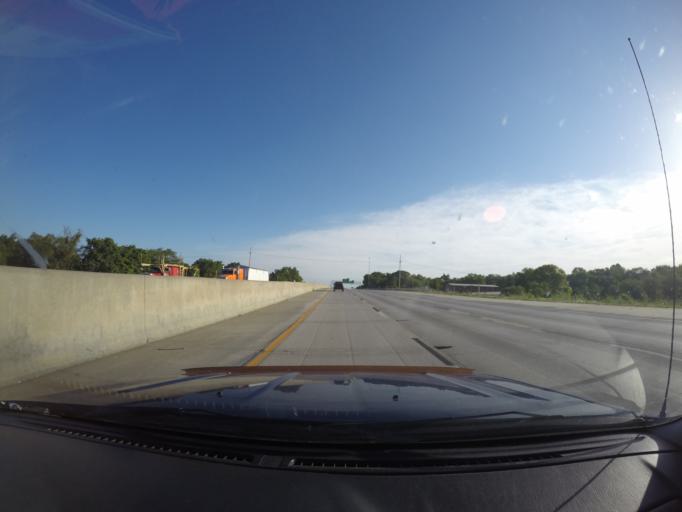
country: US
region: Kansas
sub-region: Wyandotte County
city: Kansas City
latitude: 39.1241
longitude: -94.6774
